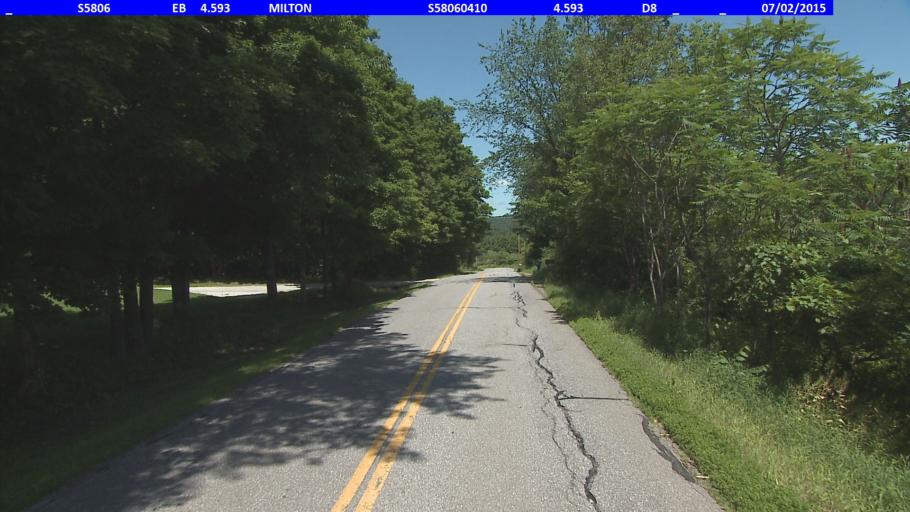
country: US
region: Vermont
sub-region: Chittenden County
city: Milton
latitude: 44.6870
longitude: -73.1768
